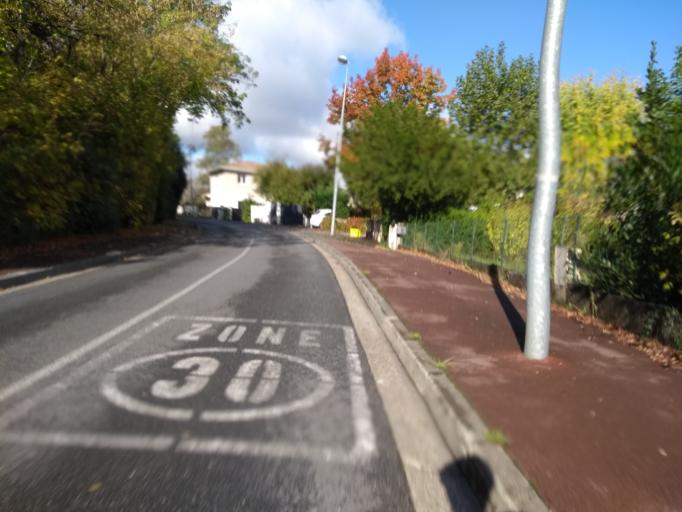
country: FR
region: Aquitaine
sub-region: Departement de la Gironde
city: Canejan
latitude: 44.7673
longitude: -0.6536
